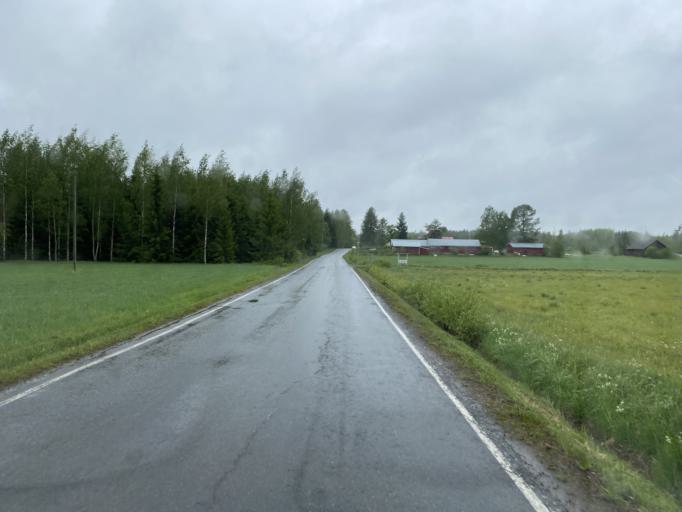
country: FI
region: Pirkanmaa
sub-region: Etelae-Pirkanmaa
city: Urjala
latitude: 60.9647
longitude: 23.5161
